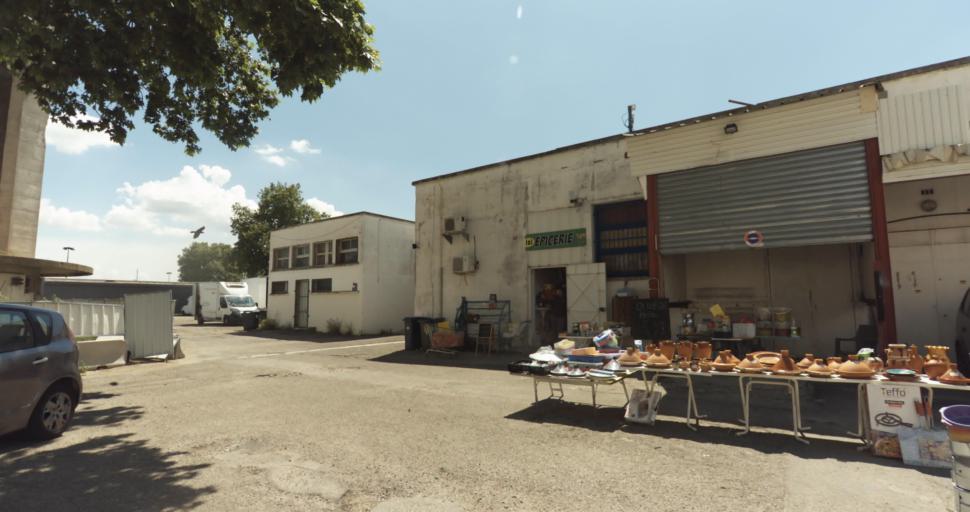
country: FR
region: Languedoc-Roussillon
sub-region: Departement du Gard
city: Milhaud
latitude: 43.8087
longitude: 4.3236
